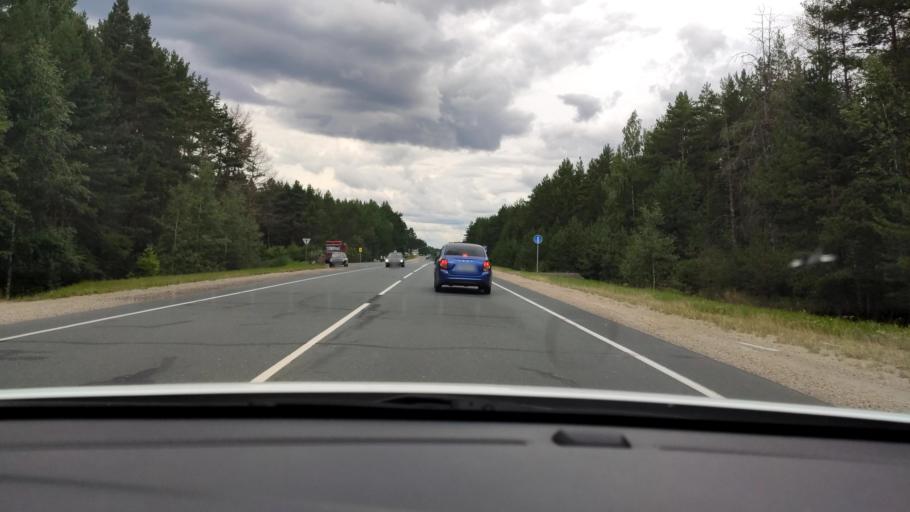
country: RU
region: Mariy-El
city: Krasnogorskiy
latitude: 56.0728
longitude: 48.3618
